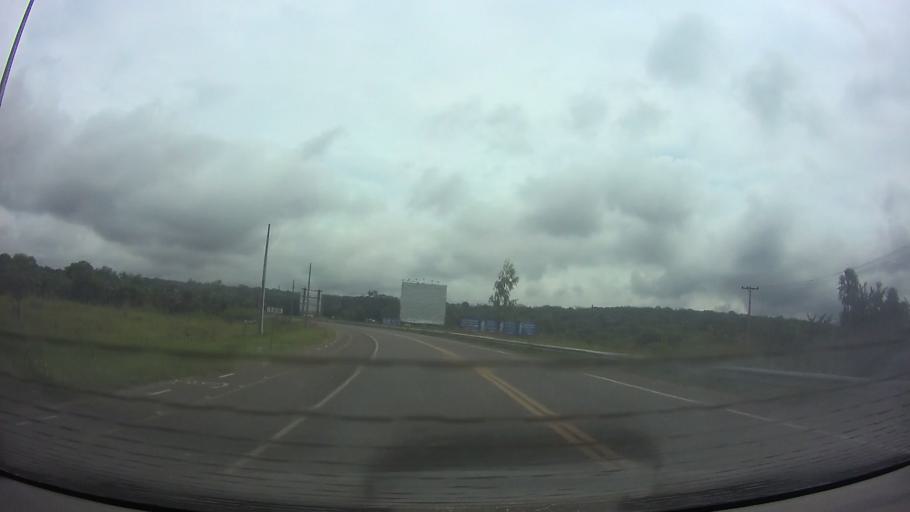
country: PY
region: Central
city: Limpio
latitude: -25.2099
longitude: -57.4137
